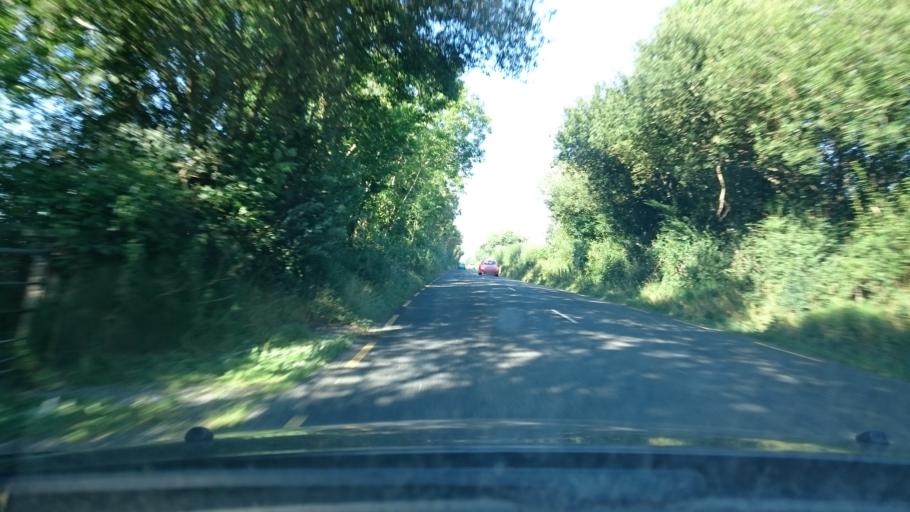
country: IE
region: Leinster
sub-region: Kilkenny
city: Graiguenamanagh
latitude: 52.5583
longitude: -6.9540
